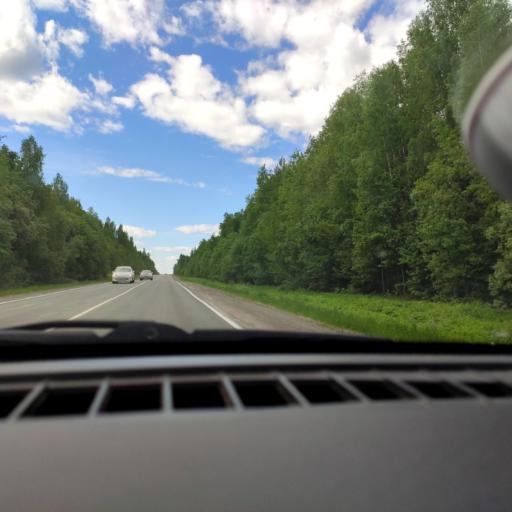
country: RU
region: Perm
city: Perm
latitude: 58.1739
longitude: 56.2318
